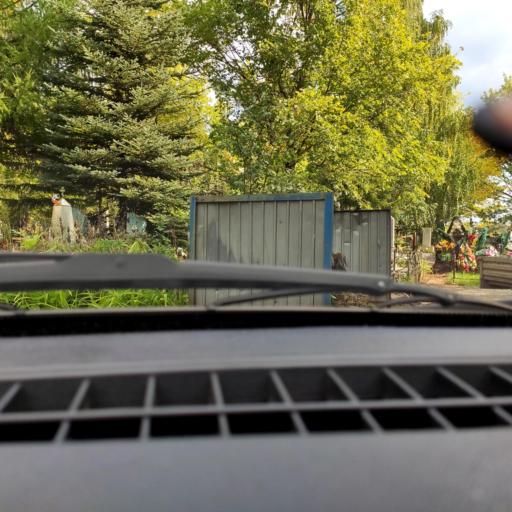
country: RU
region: Bashkortostan
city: Ufa
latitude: 54.8522
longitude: 56.1622
